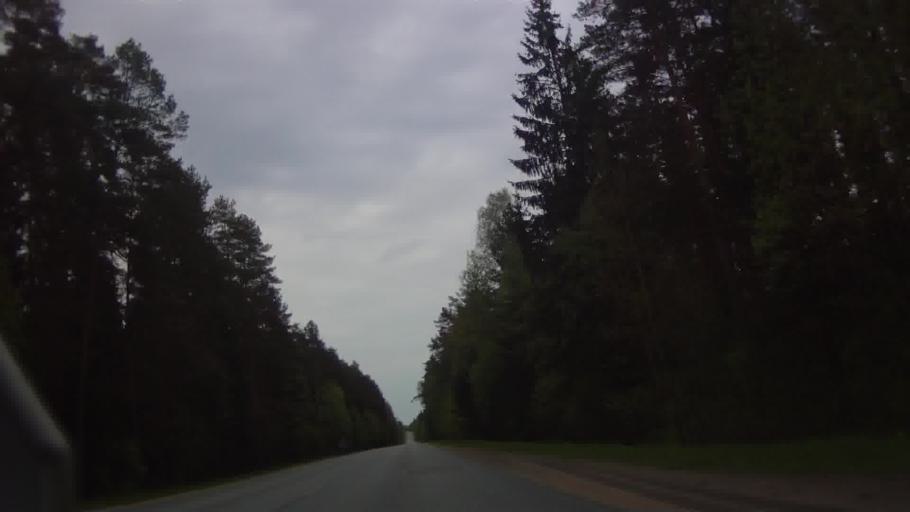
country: LV
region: Incukalns
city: Incukalns
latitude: 57.1149
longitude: 24.6594
